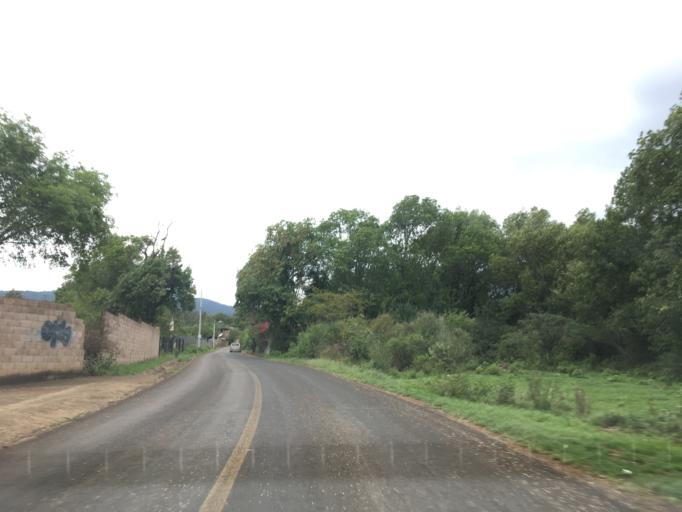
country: MX
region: Michoacan
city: Acuitzio del Canje
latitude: 19.5580
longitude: -101.2730
